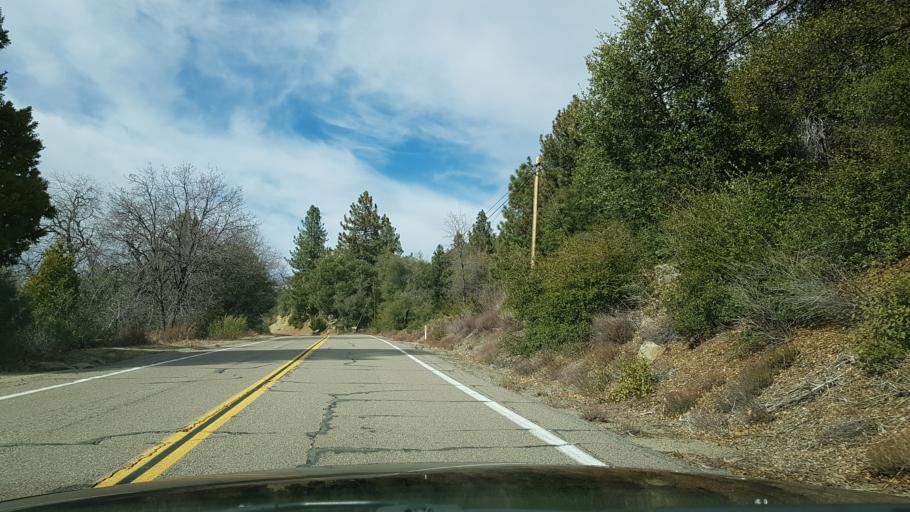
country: US
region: California
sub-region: Riverside County
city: Aguanga
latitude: 33.3556
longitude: -116.8698
